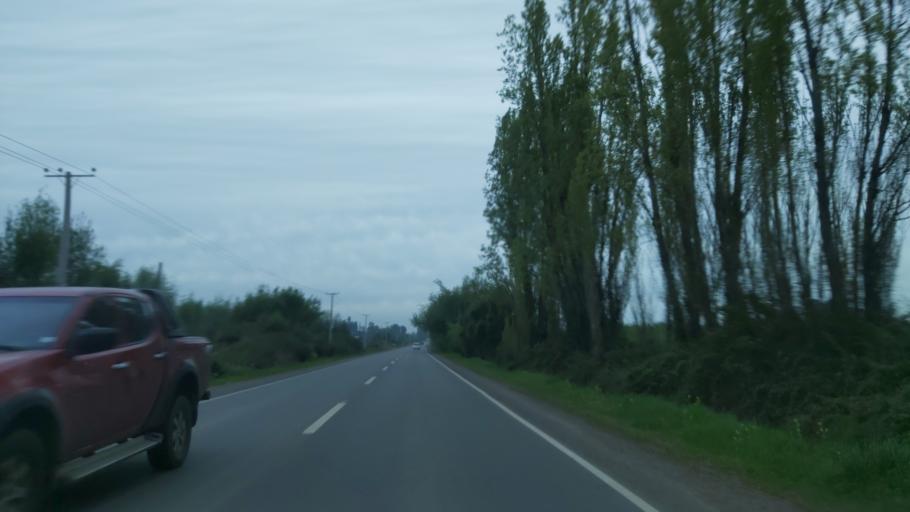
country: CL
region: Maule
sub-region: Provincia de Linares
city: Colbun
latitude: -35.7432
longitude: -71.4919
